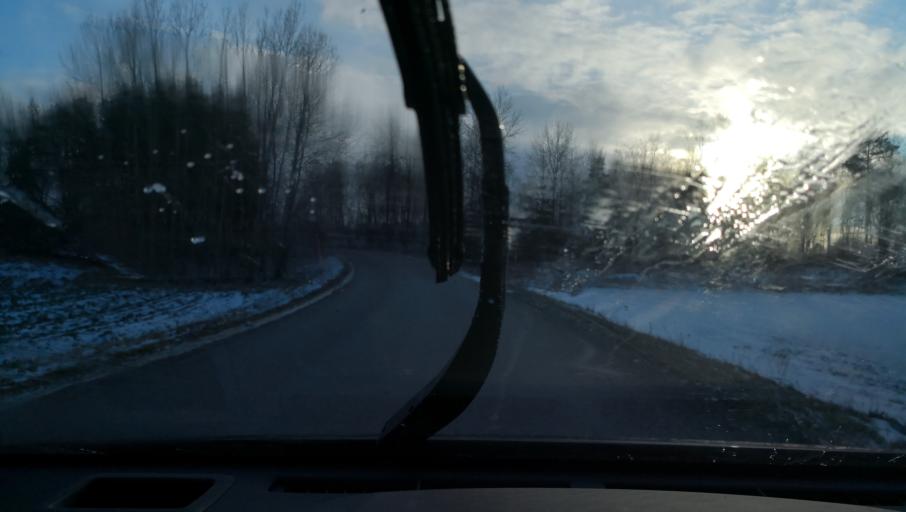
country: SE
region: Vaestmanland
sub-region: Vasteras
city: Tillberga
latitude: 59.6544
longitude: 16.7558
